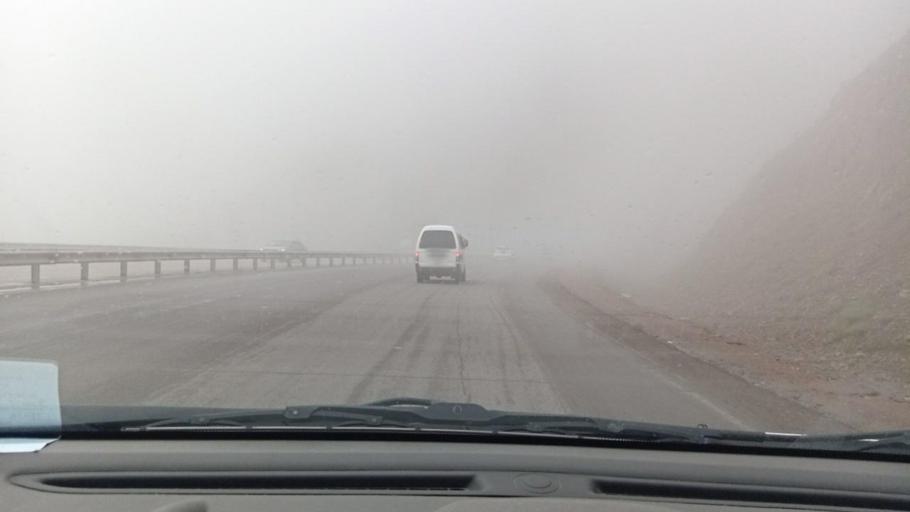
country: UZ
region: Toshkent
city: Angren
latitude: 41.1059
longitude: 70.5098
